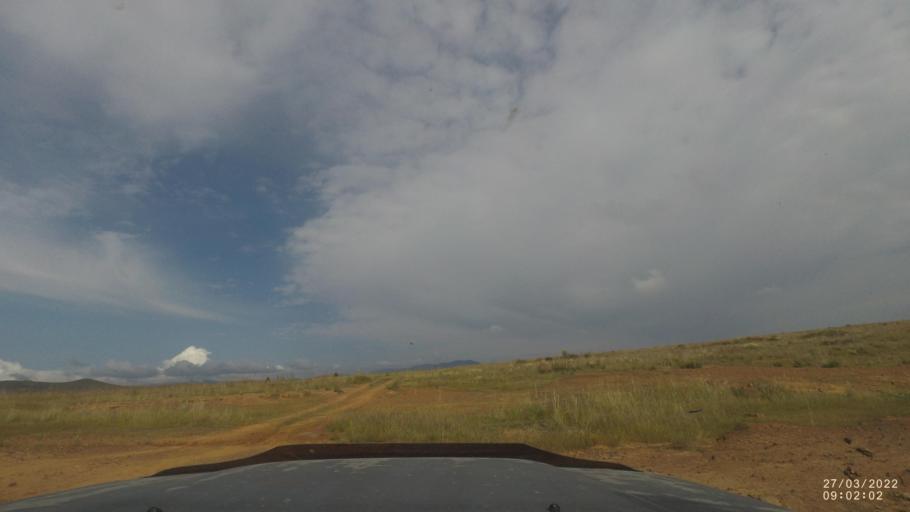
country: BO
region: Cochabamba
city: Cliza
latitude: -17.7372
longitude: -65.8565
